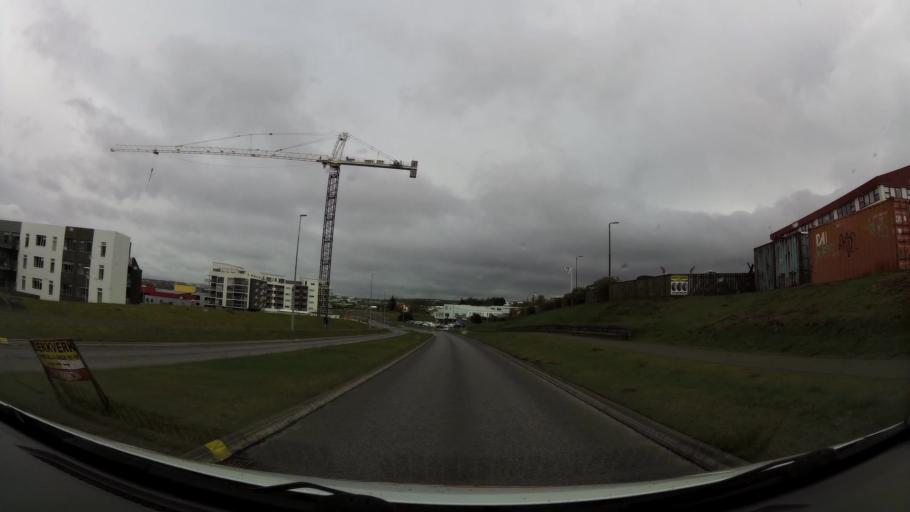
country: IS
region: Capital Region
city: Gardabaer
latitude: 64.0916
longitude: -21.9415
